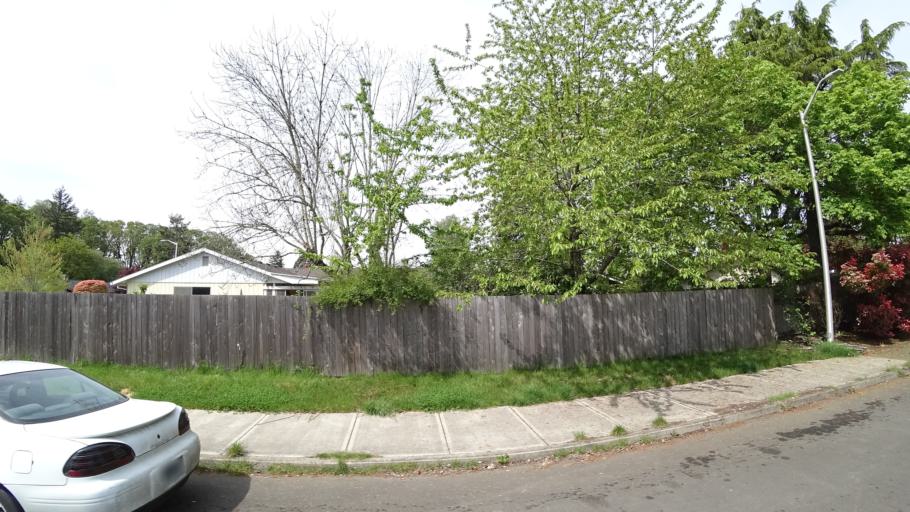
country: US
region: Oregon
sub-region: Washington County
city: Hillsboro
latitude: 45.5282
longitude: -122.9585
